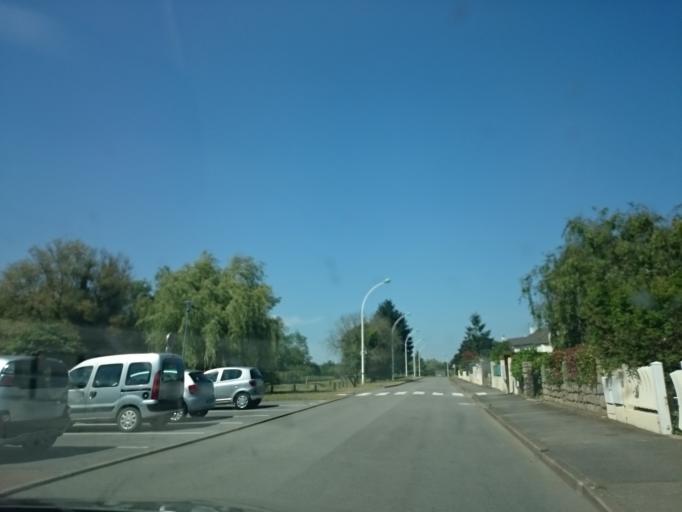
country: FR
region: Pays de la Loire
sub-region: Departement de la Loire-Atlantique
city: Indre
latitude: 47.2015
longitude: -1.6746
